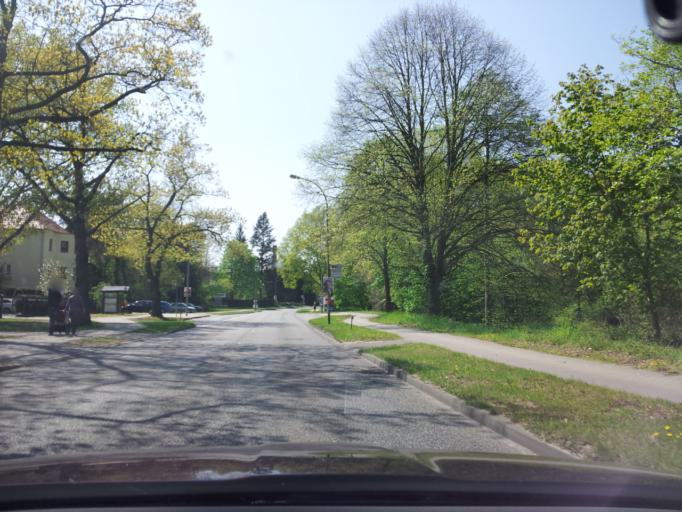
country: DE
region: Brandenburg
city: Kleinmachnow
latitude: 52.3923
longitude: 13.2317
